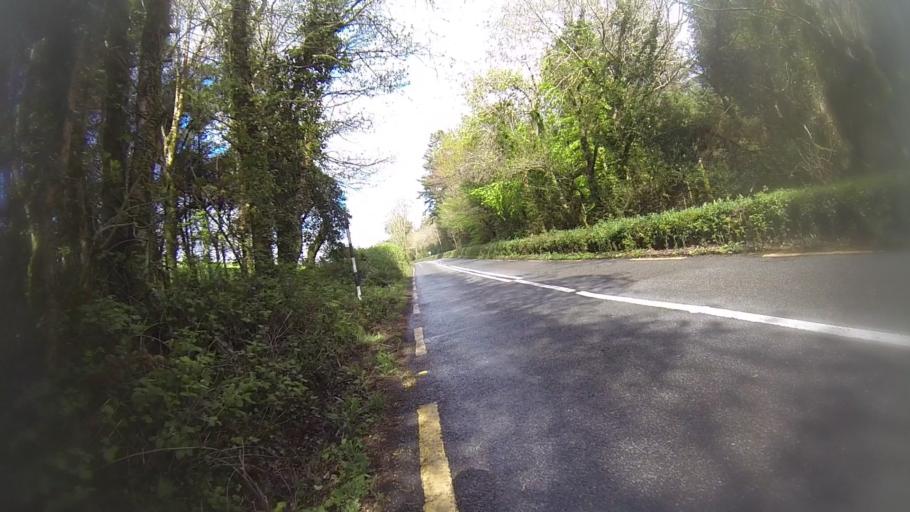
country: IE
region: Munster
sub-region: Ciarrai
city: Kenmare
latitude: 51.8509
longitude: -9.7401
